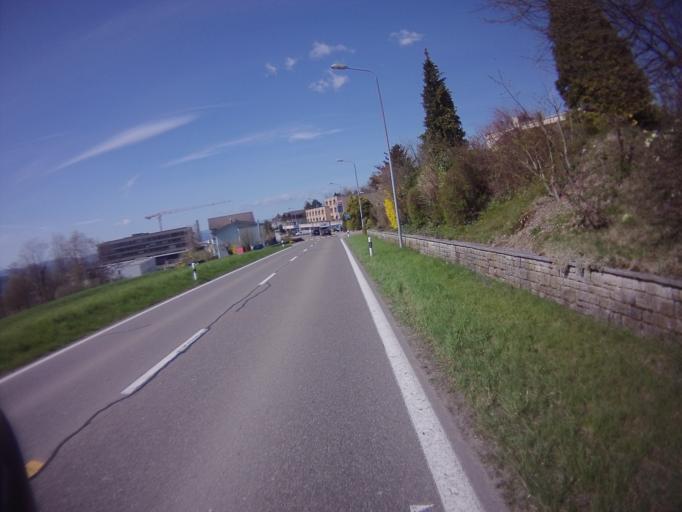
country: CH
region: Aargau
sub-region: Bezirk Baden
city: Kunten
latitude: 47.3859
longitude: 8.3467
